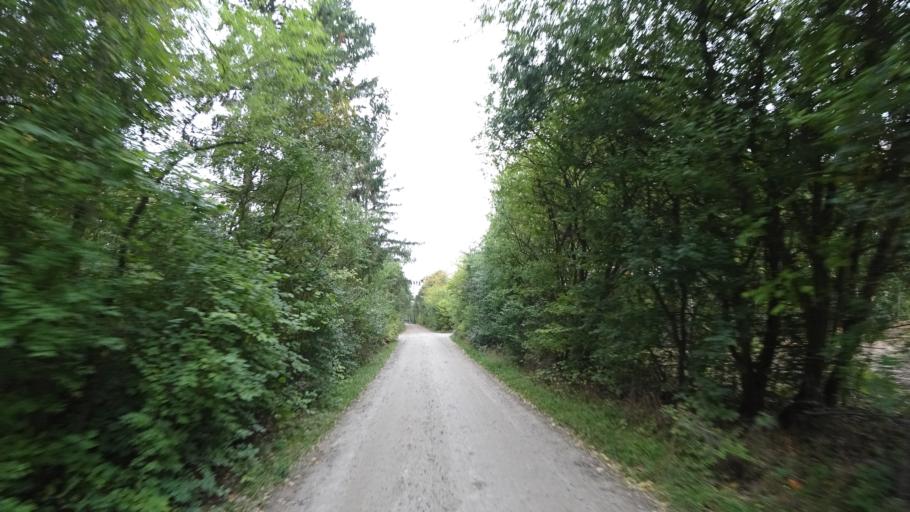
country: SE
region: Skane
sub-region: Kavlinge Kommun
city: Hofterup
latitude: 55.8232
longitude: 12.9619
